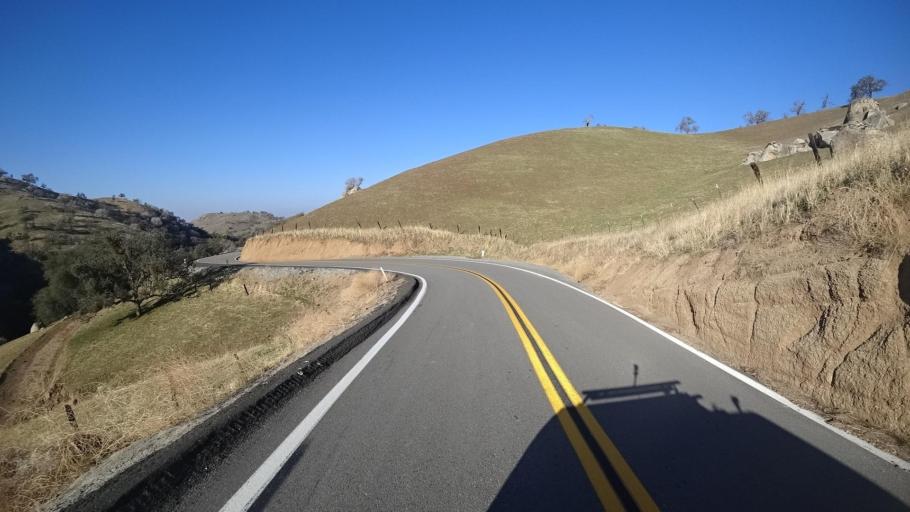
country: US
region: California
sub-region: Kern County
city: Alta Sierra
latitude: 35.7147
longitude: -118.8126
